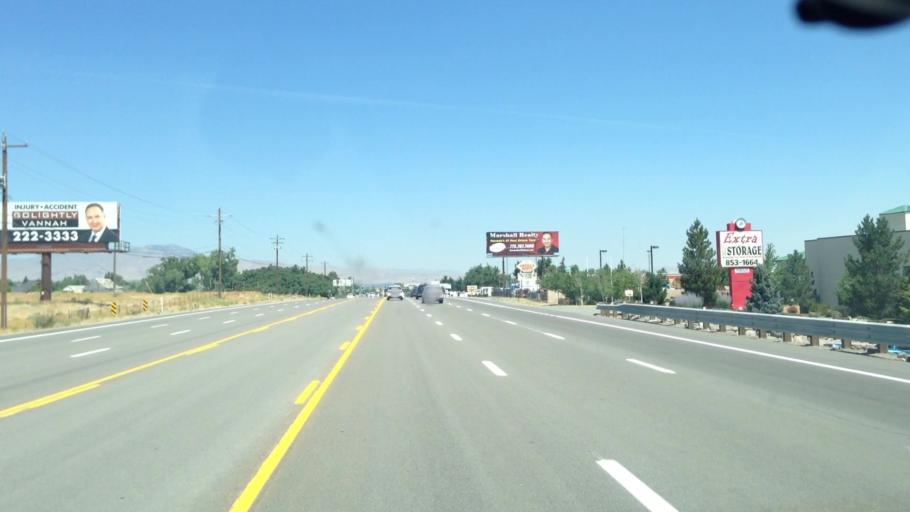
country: US
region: Nevada
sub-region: Washoe County
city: Sparks
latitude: 39.4348
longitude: -119.7668
